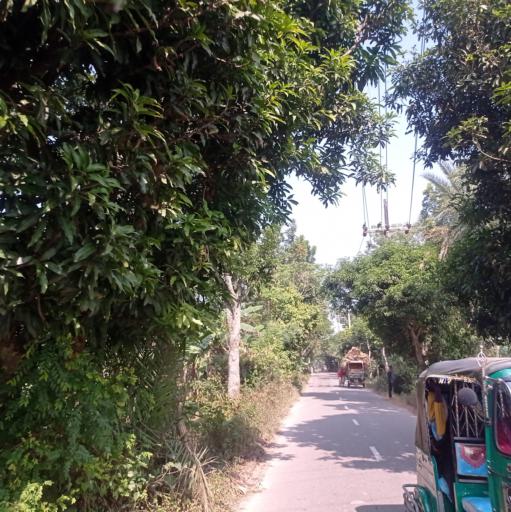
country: BD
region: Dhaka
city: Narsingdi
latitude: 24.0372
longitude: 90.6763
